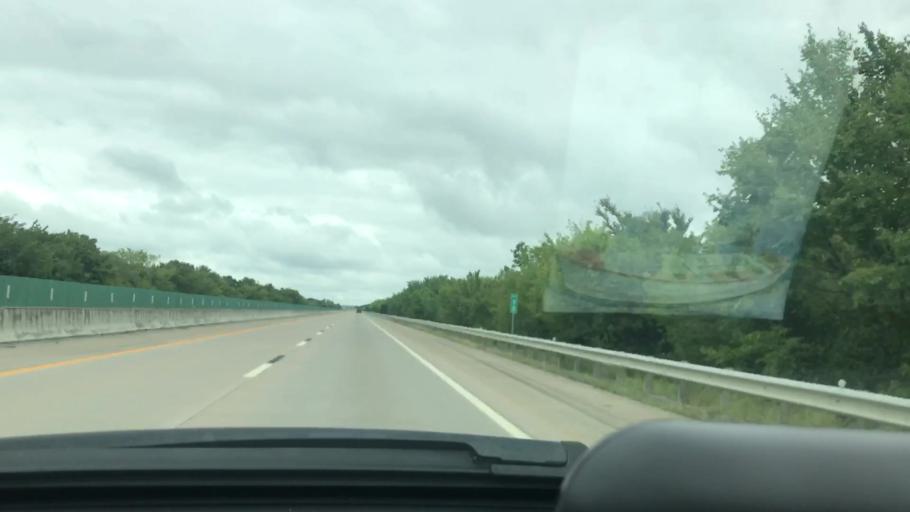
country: US
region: Oklahoma
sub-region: Pittsburg County
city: Krebs
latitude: 35.0182
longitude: -95.7177
